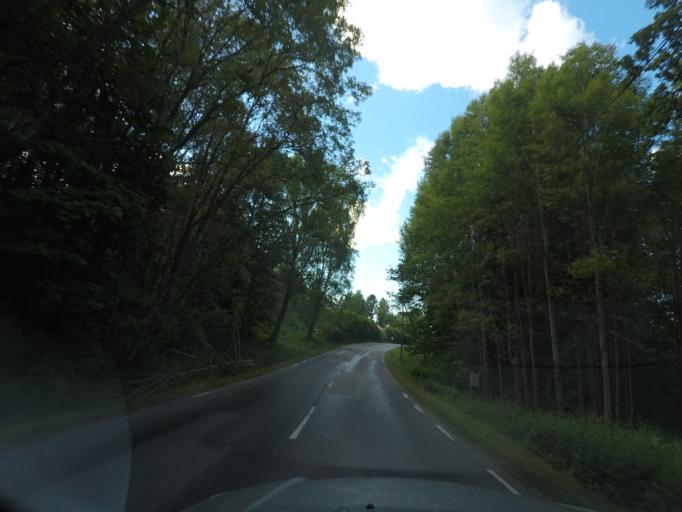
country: SE
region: Stockholm
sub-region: Sigtuna Kommun
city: Marsta
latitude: 59.6956
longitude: 17.9748
